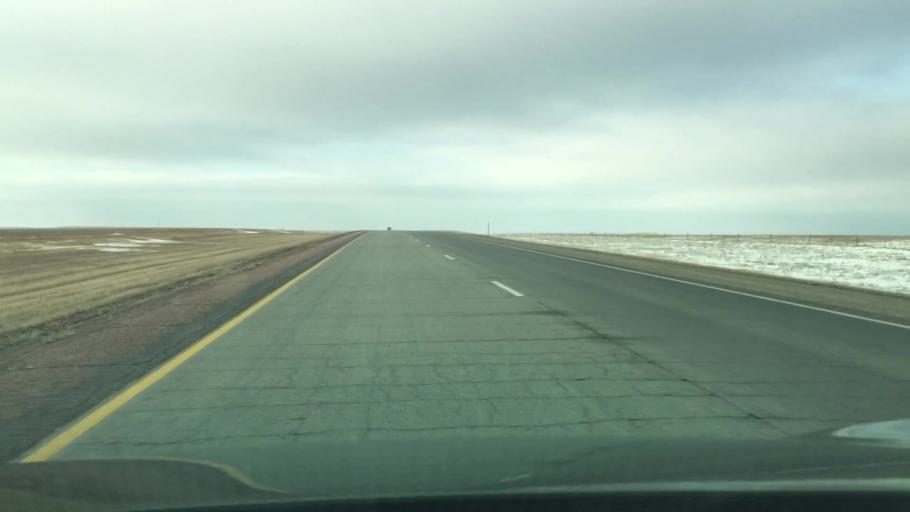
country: US
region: South Dakota
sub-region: Brule County
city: Chamberlain
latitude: 43.8354
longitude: -99.4711
